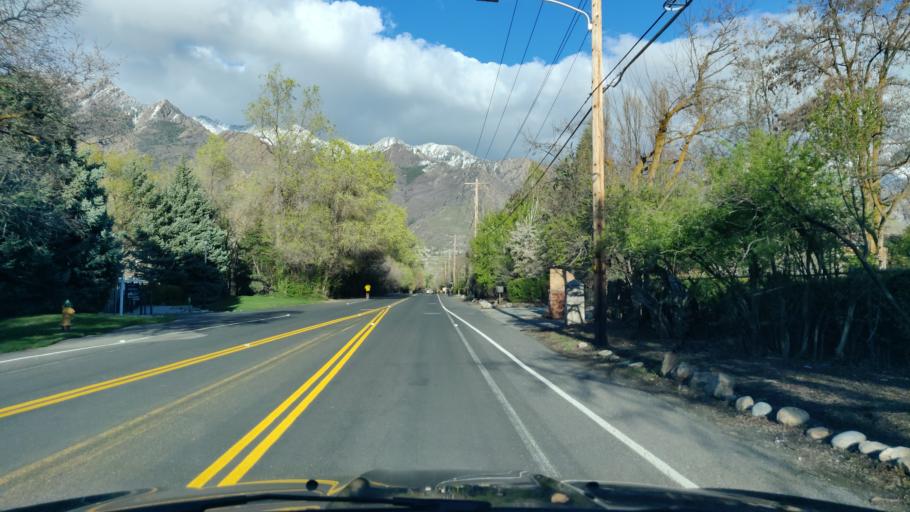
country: US
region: Utah
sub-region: Salt Lake County
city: Cottonwood Heights
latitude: 40.6385
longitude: -111.8230
